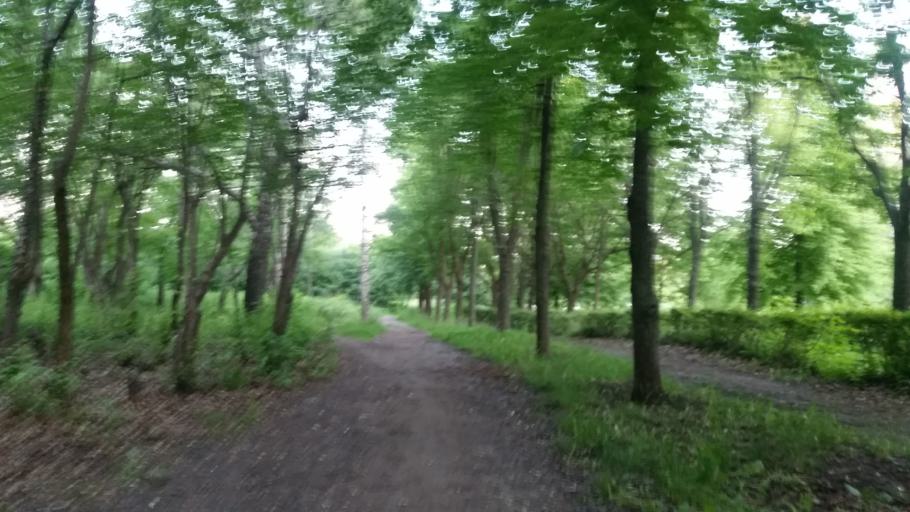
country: RU
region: Ulyanovsk
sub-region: Ulyanovskiy Rayon
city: Ulyanovsk
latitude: 54.3441
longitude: 48.3979
